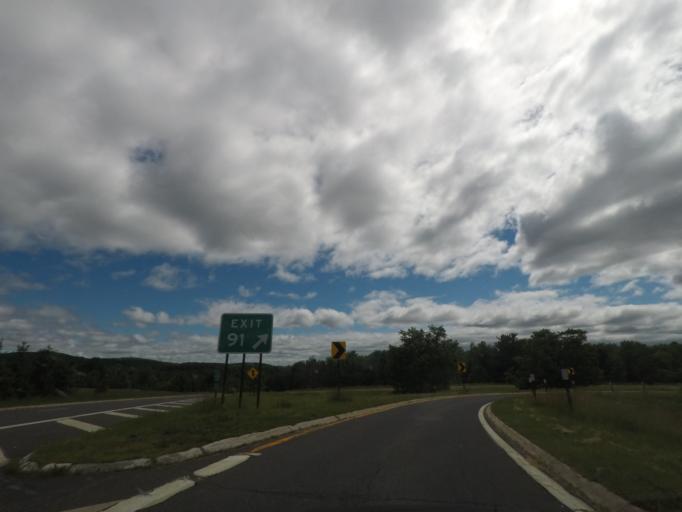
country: US
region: New York
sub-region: Columbia County
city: Philmont
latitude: 42.2555
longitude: -73.6148
